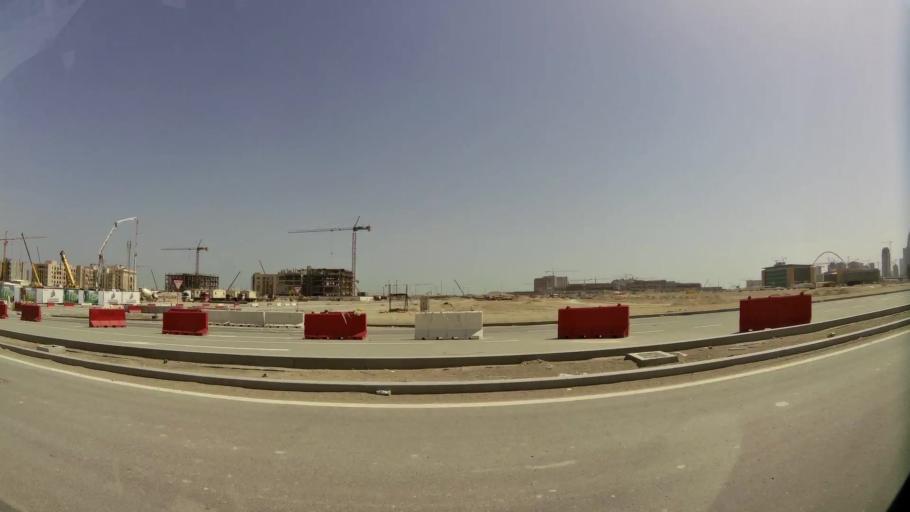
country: QA
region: Baladiyat Umm Salal
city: Umm Salal Muhammad
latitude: 25.4063
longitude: 51.5063
